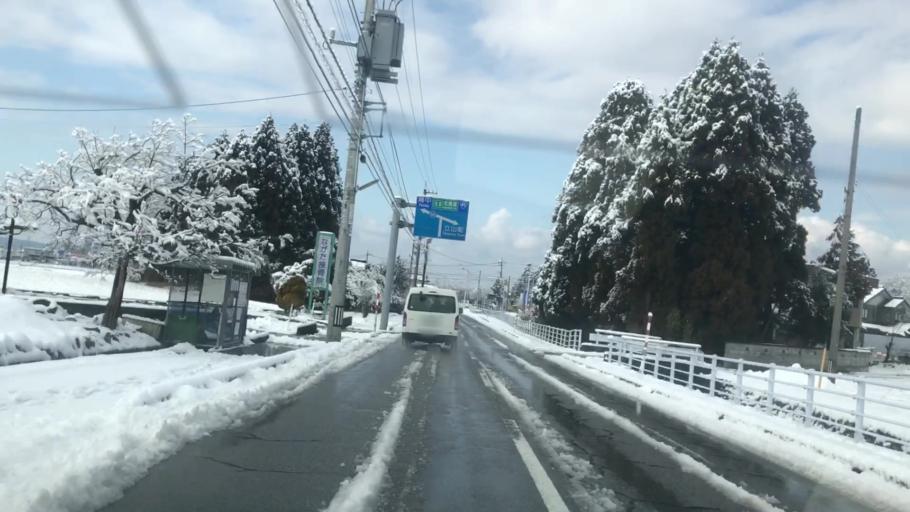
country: JP
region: Toyama
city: Toyama-shi
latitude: 36.6288
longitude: 137.2371
